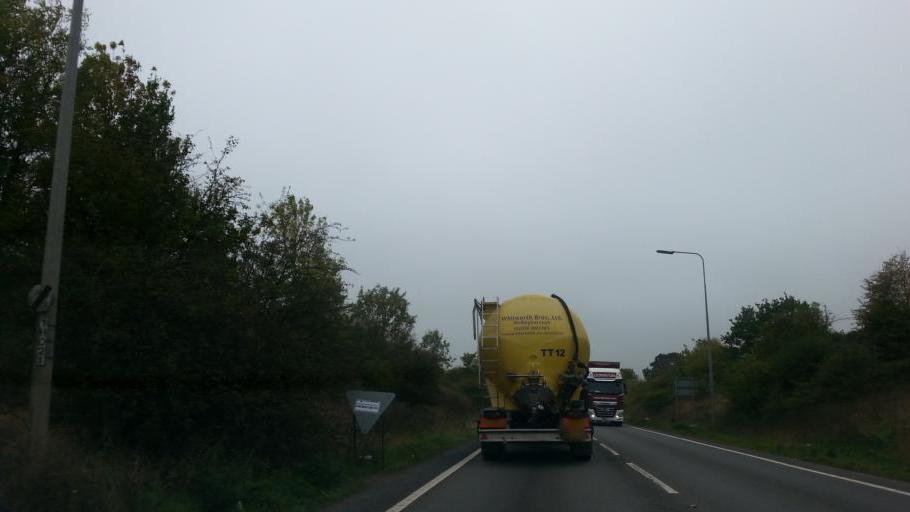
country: GB
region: England
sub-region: Northamptonshire
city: Thrapston
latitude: 52.3903
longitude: -0.5234
